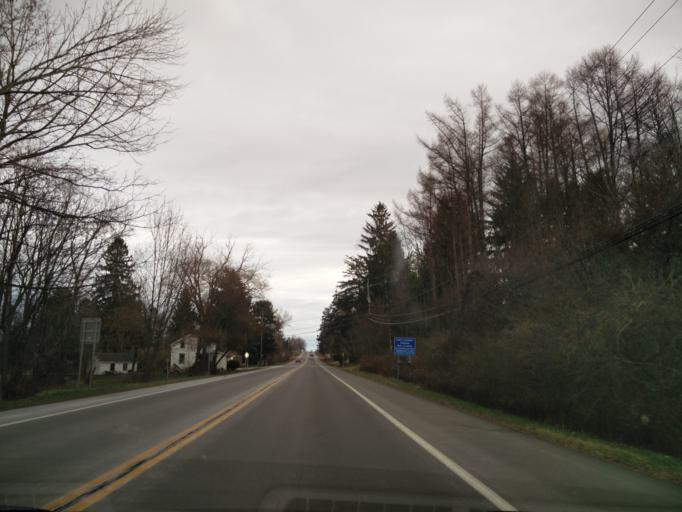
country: US
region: New York
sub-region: Tompkins County
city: Trumansburg
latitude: 42.5059
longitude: -76.6115
